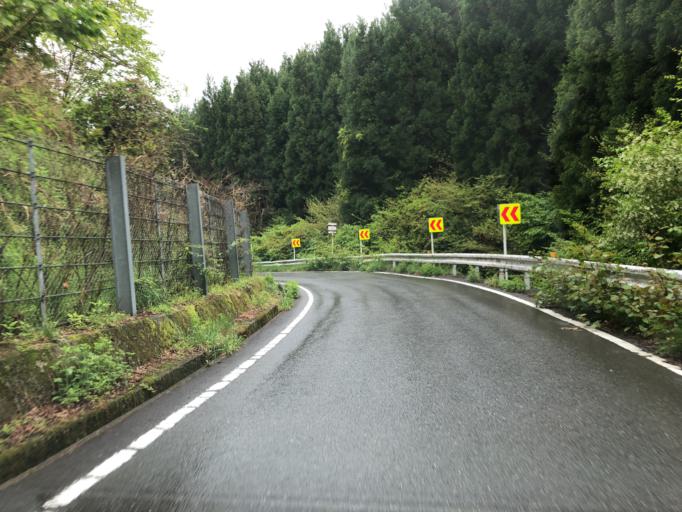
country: JP
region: Fukushima
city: Ishikawa
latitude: 37.0014
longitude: 140.6059
